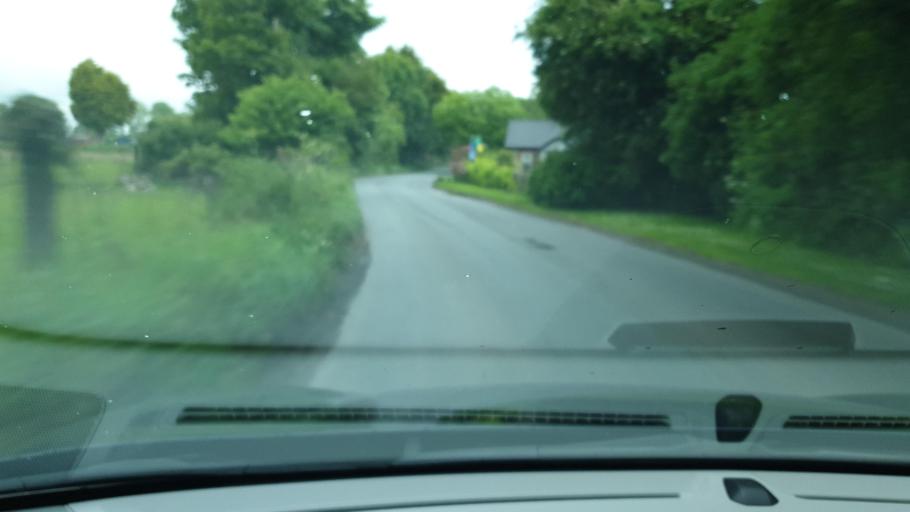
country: IE
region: Leinster
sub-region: An Mhi
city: Ashbourne
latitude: 53.5558
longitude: -6.3966
